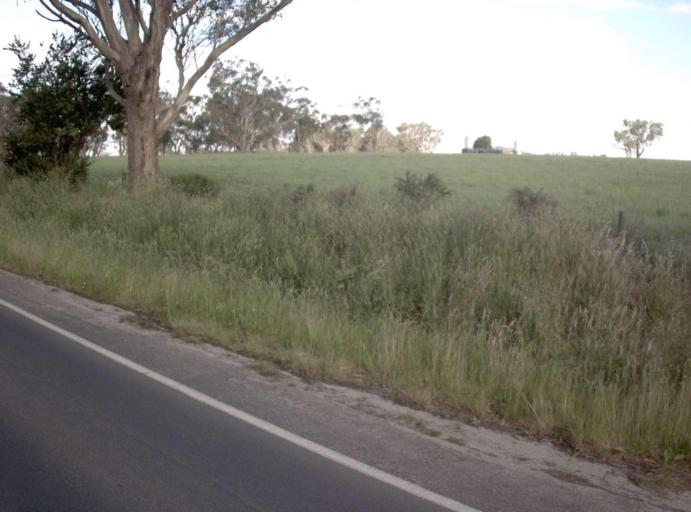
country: AU
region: Victoria
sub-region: Bass Coast
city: North Wonthaggi
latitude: -38.5834
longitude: 145.8169
